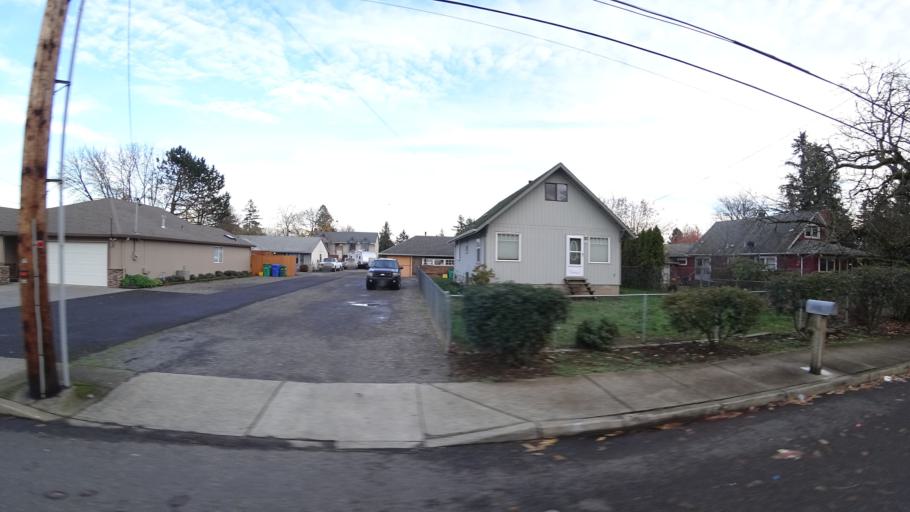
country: US
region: Oregon
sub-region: Multnomah County
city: Lents
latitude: 45.5161
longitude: -122.5210
